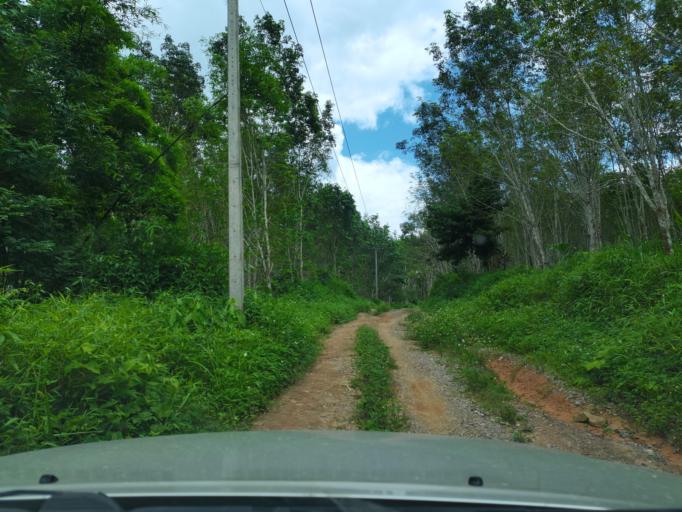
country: LA
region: Loungnamtha
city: Muang Long
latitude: 20.6965
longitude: 101.0391
